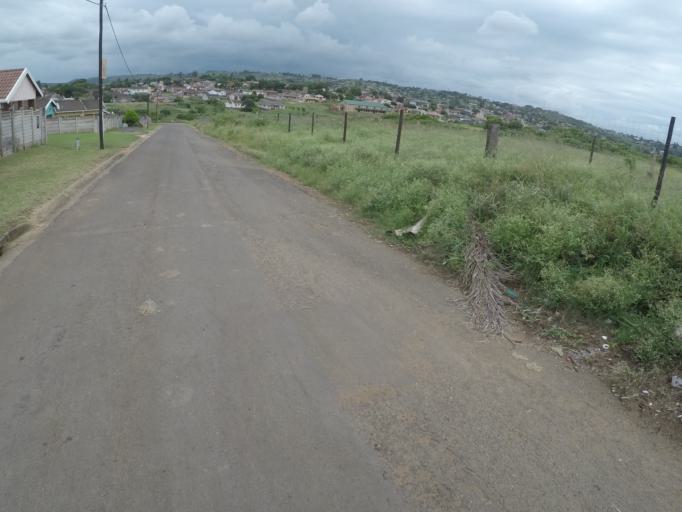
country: ZA
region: KwaZulu-Natal
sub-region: uThungulu District Municipality
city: Empangeni
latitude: -28.7828
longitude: 31.8542
